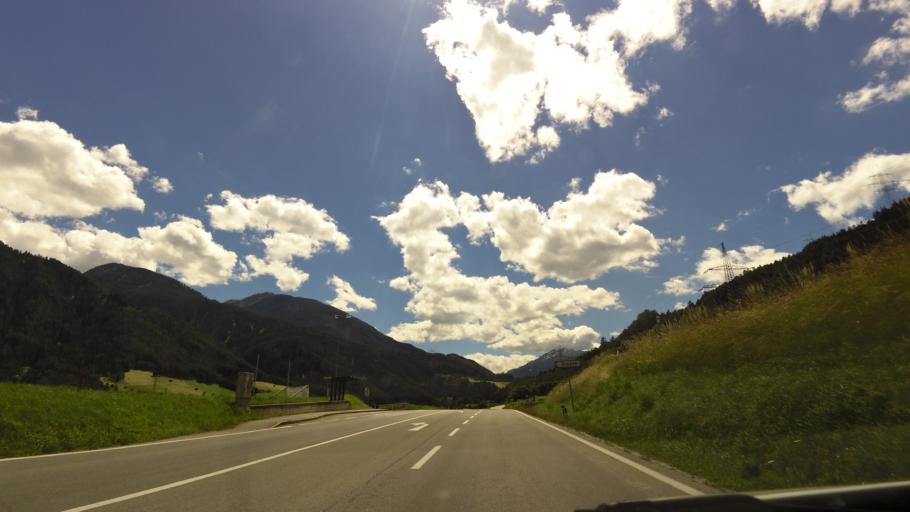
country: AT
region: Tyrol
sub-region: Politischer Bezirk Imst
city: Roppen
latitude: 47.2215
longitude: 10.8152
